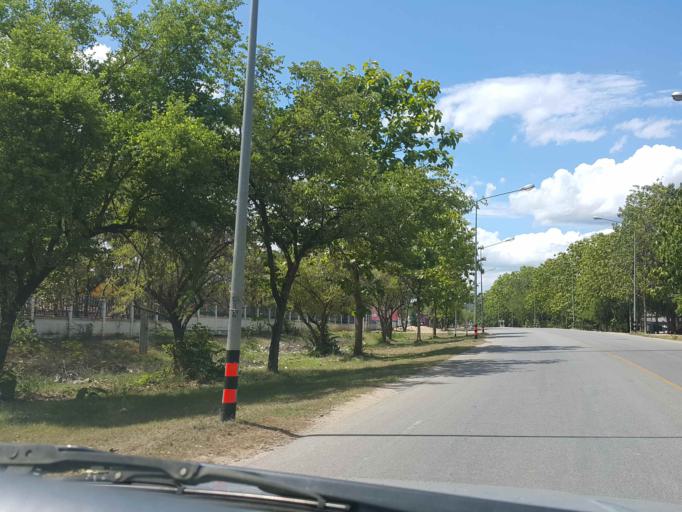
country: TH
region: Chiang Mai
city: Chom Thong
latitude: 18.4574
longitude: 98.6752
